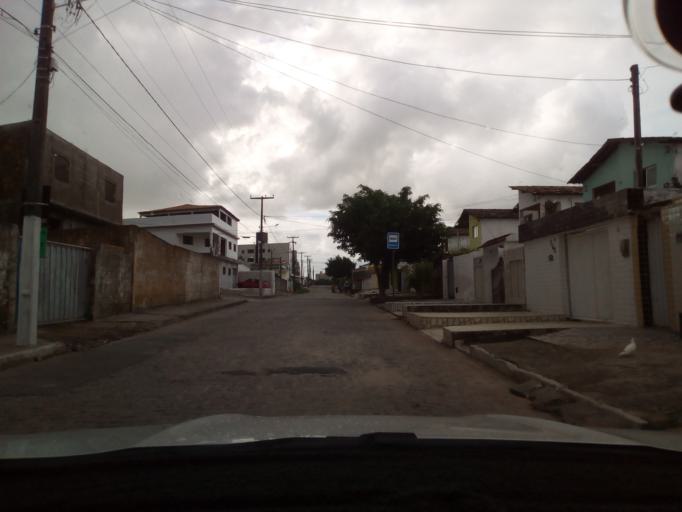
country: BR
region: Paraiba
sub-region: Joao Pessoa
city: Joao Pessoa
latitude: -7.1709
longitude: -34.8893
